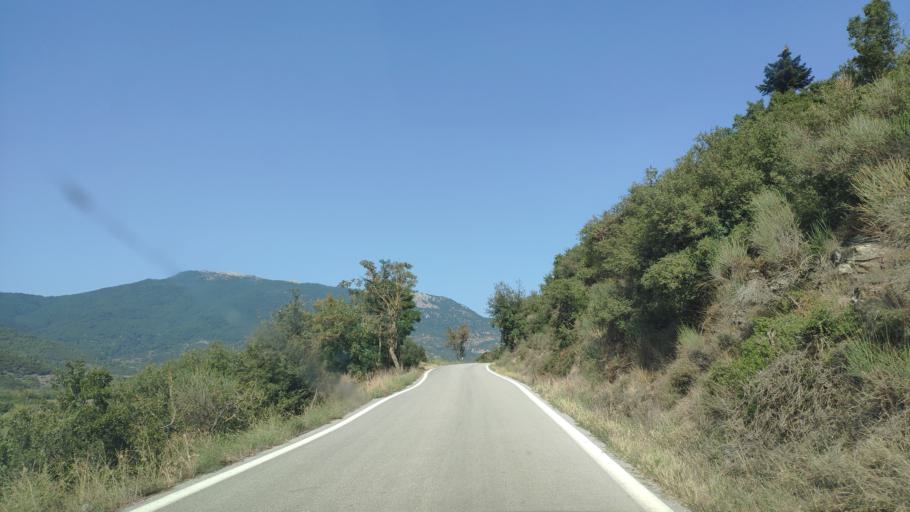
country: GR
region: West Greece
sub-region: Nomos Achaias
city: Aiyira
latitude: 37.9171
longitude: 22.3311
